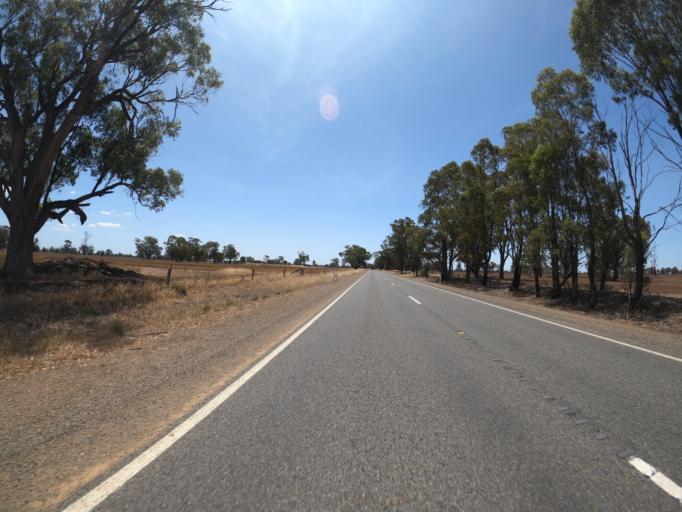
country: AU
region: Victoria
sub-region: Moira
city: Yarrawonga
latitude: -36.2049
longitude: 145.9672
